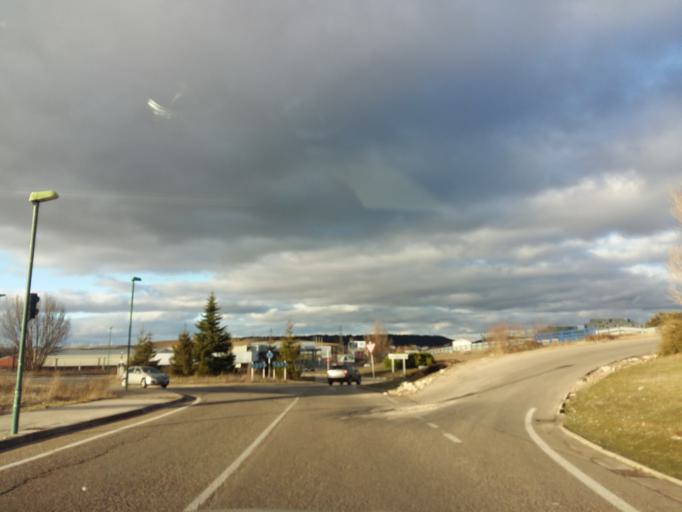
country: ES
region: Castille and Leon
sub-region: Provincia de Burgos
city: Burgos
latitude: 42.3226
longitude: -3.7014
